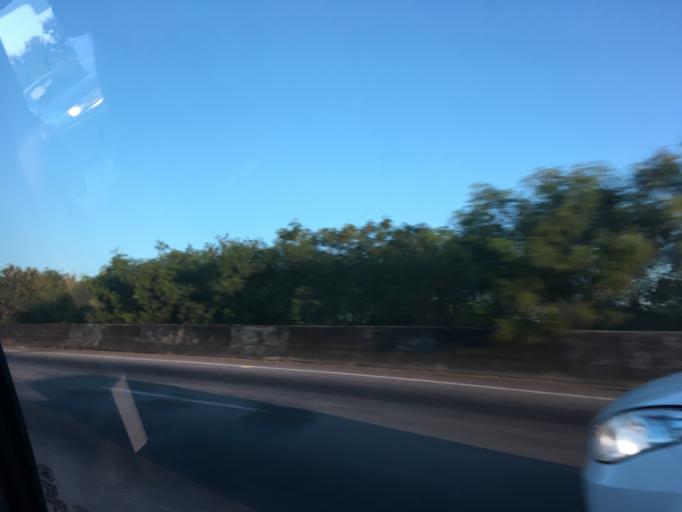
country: BR
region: Rio de Janeiro
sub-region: Duque De Caxias
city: Duque de Caxias
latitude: -22.8078
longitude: -43.2919
